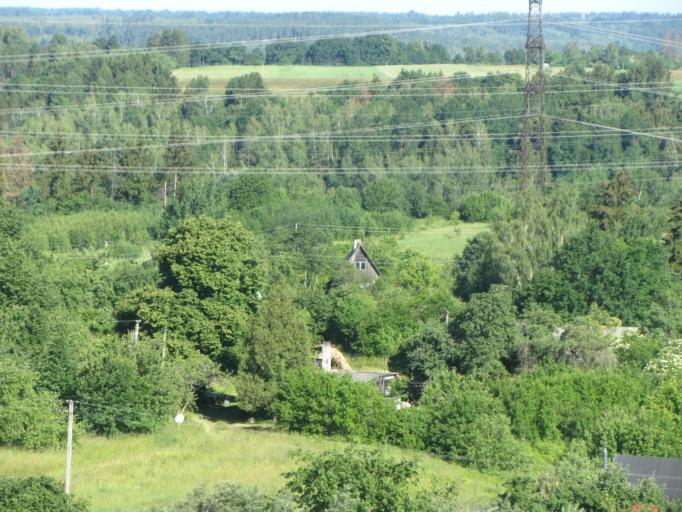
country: LT
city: Ziezmariai
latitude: 54.8003
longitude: 24.2679
